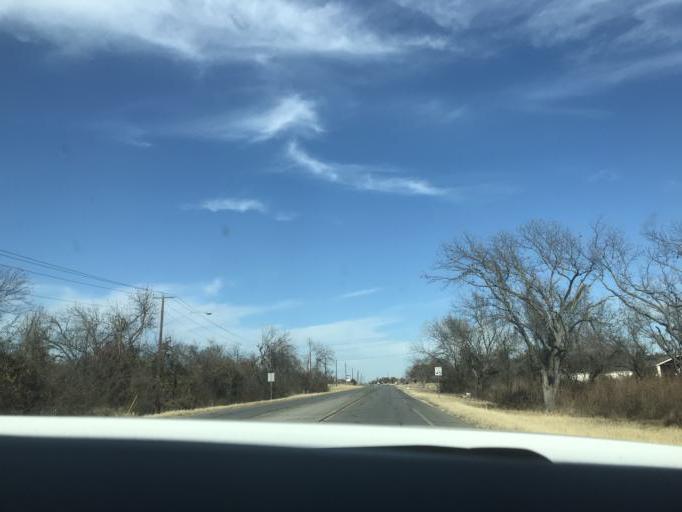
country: US
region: Texas
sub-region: Erath County
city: Stephenville
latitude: 32.2123
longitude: -98.2454
